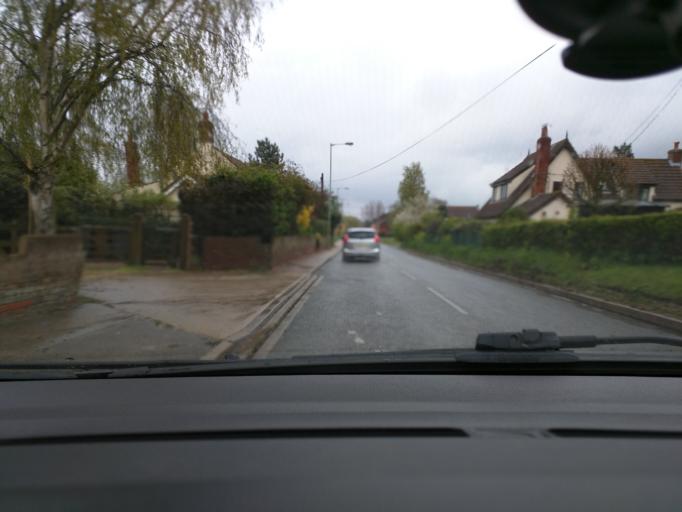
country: GB
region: England
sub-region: Suffolk
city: Leiston
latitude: 52.1903
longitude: 1.5571
